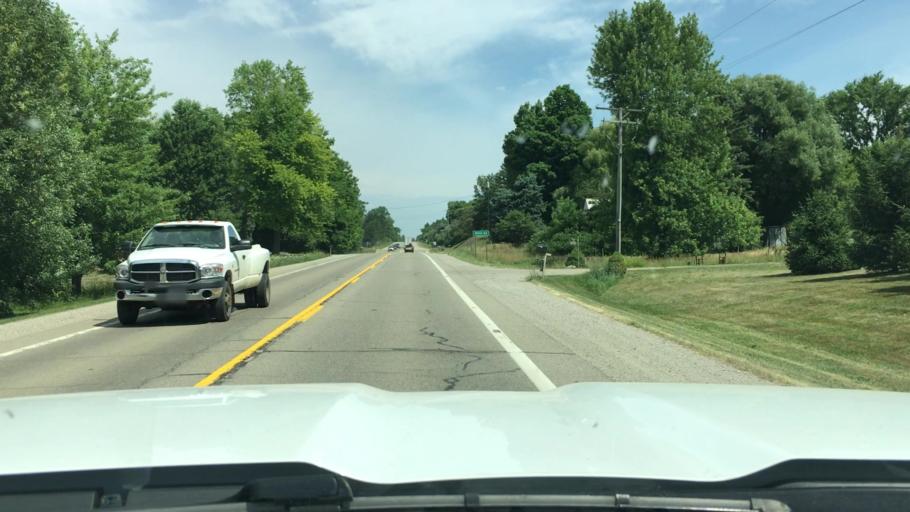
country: US
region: Michigan
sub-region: Sanilac County
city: Brown City
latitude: 43.1644
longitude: -83.0756
